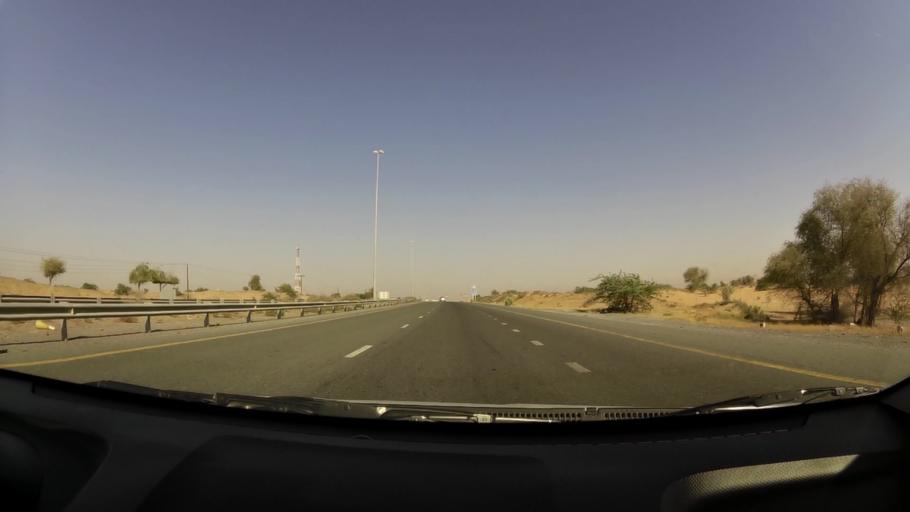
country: AE
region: Umm al Qaywayn
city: Umm al Qaywayn
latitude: 25.4475
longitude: 55.6203
